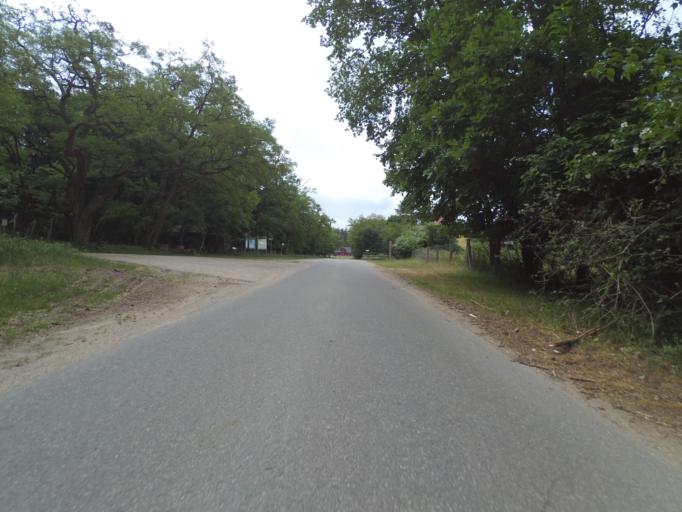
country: DE
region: Mecklenburg-Vorpommern
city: Malchow
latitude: 53.5687
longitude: 12.3668
